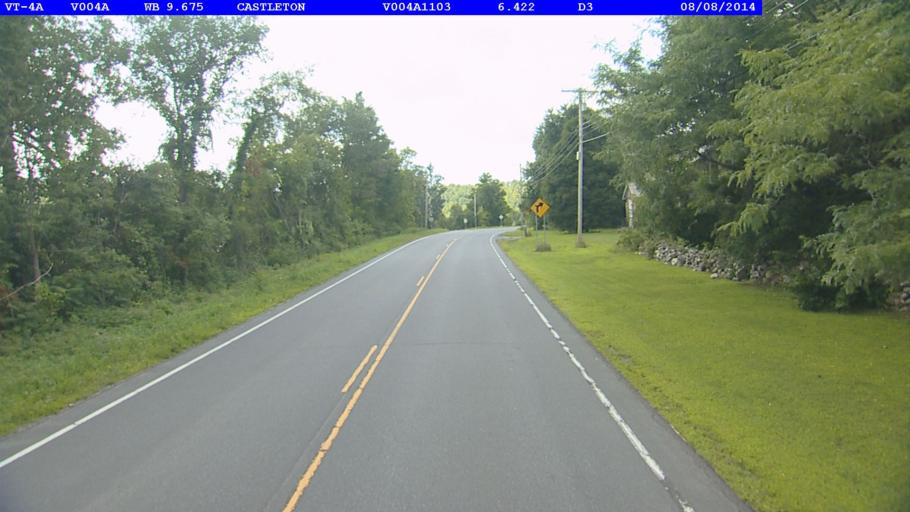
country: US
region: Vermont
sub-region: Rutland County
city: Castleton
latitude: 43.6101
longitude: -73.1227
